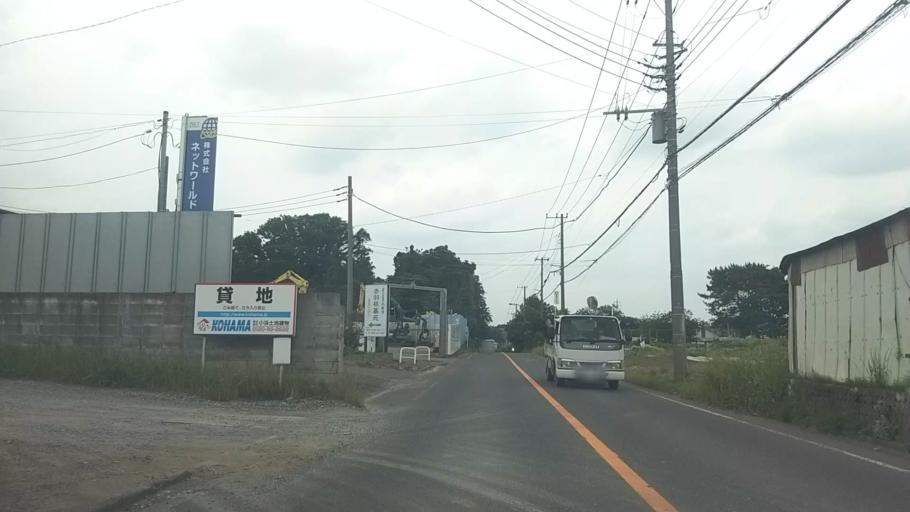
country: JP
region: Kanagawa
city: Fujisawa
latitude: 35.3531
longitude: 139.4352
